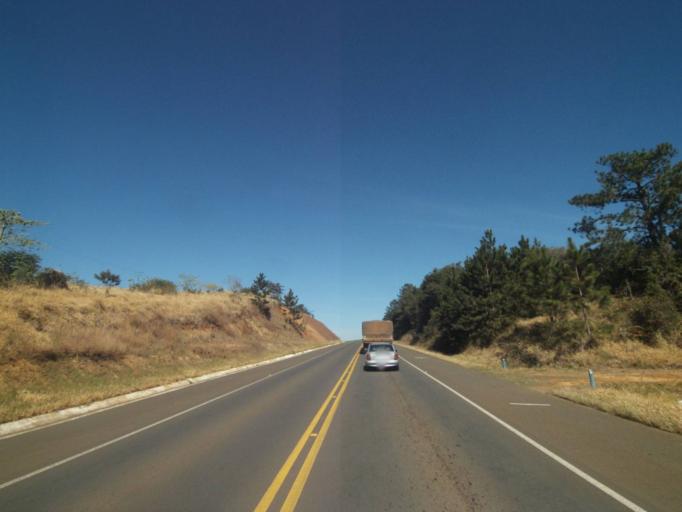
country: BR
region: Parana
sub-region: Tibagi
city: Tibagi
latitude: -24.7242
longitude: -50.4510
